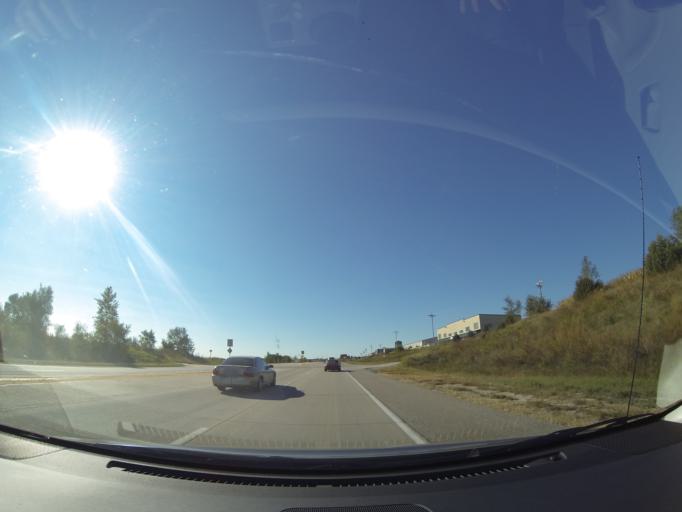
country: US
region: Nebraska
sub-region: Sarpy County
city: Gretna
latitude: 41.1110
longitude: -96.2535
